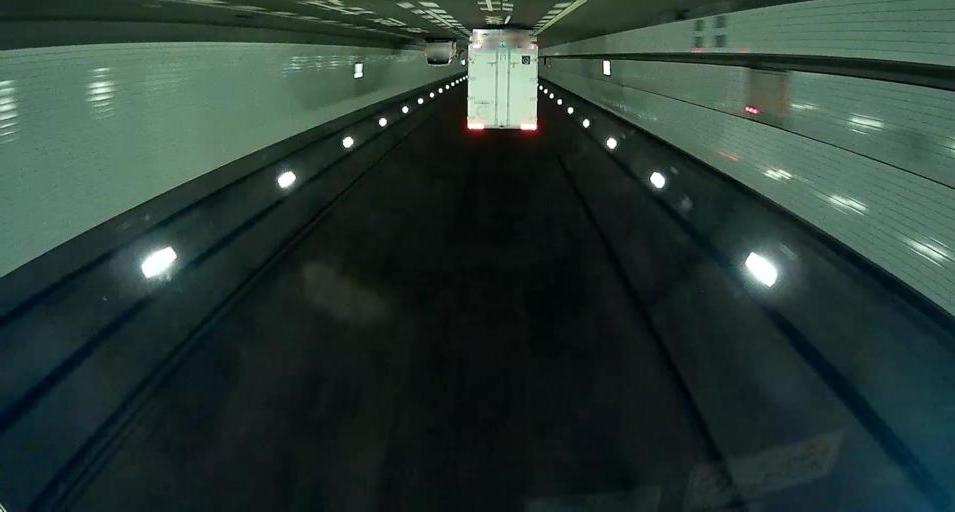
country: JP
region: Chiba
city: Kisarazu
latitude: 35.4658
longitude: 139.8721
